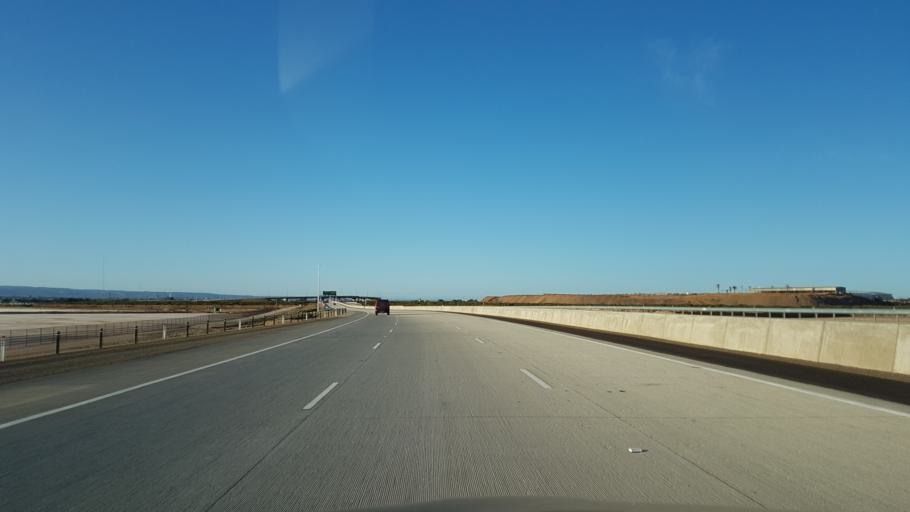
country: AU
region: South Australia
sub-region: Port Adelaide Enfield
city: Enfield
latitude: -34.8170
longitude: 138.5619
